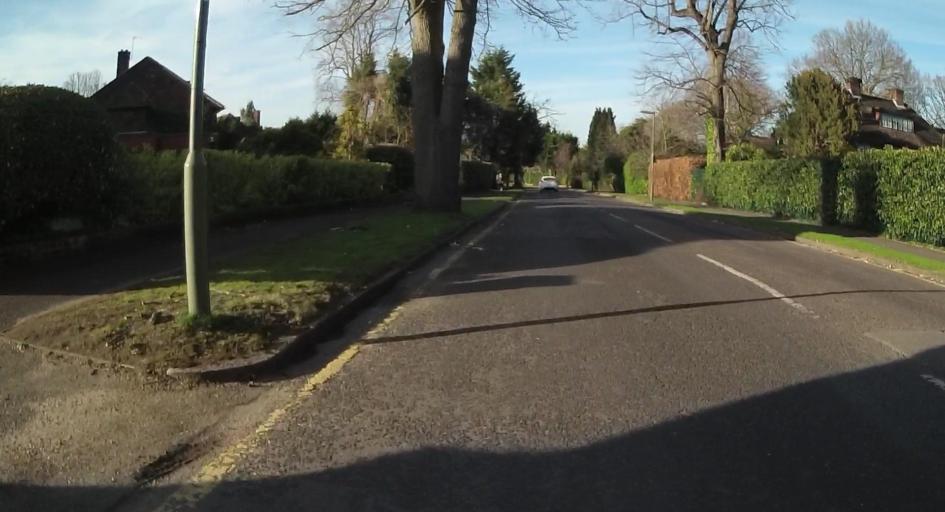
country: GB
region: England
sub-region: Surrey
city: Walton-on-Thames
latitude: 51.3771
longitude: -0.4170
